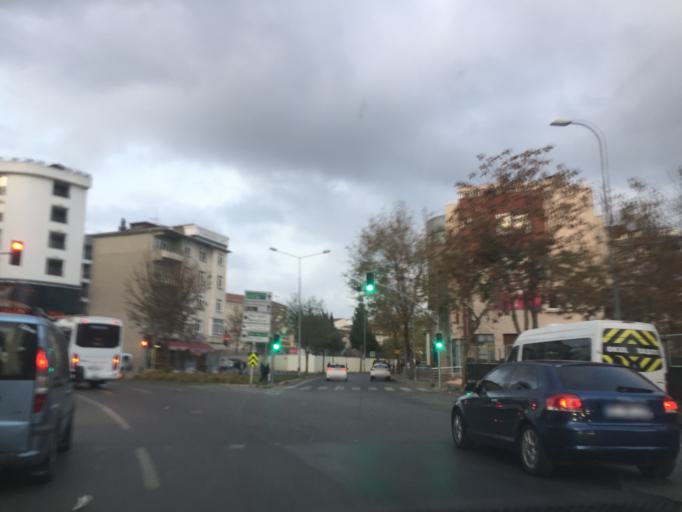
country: TR
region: Istanbul
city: Samandira
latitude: 40.9872
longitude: 29.2323
